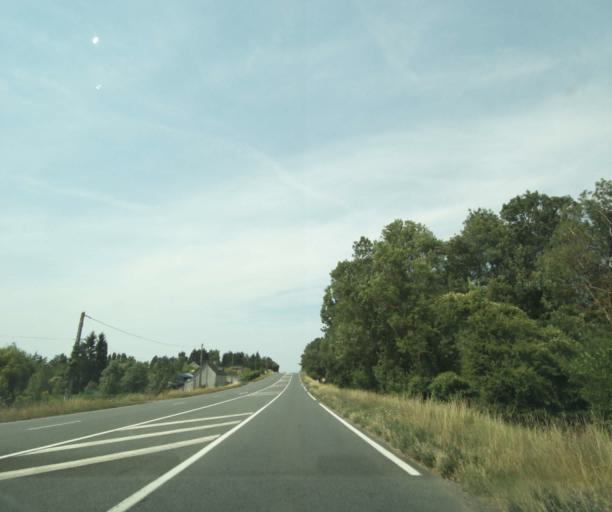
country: FR
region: Centre
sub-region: Departement d'Indre-et-Loire
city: Sainte-Maure-de-Touraine
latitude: 47.1493
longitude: 0.6467
